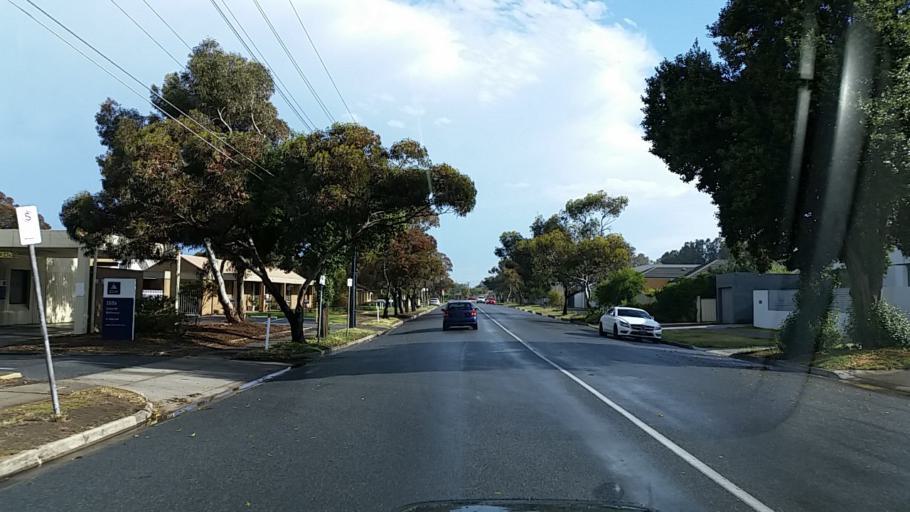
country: AU
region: South Australia
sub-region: Charles Sturt
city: Grange
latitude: -34.9107
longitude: 138.4993
